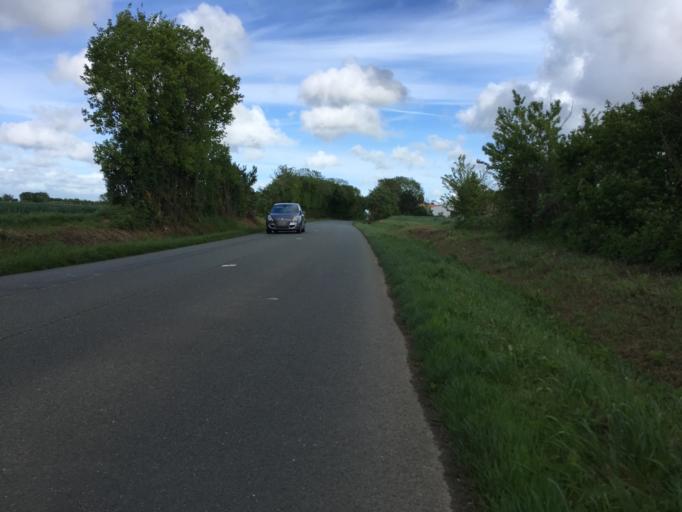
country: FR
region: Poitou-Charentes
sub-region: Departement de la Charente-Maritime
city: Bourgneuf
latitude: 46.1714
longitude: -1.0080
